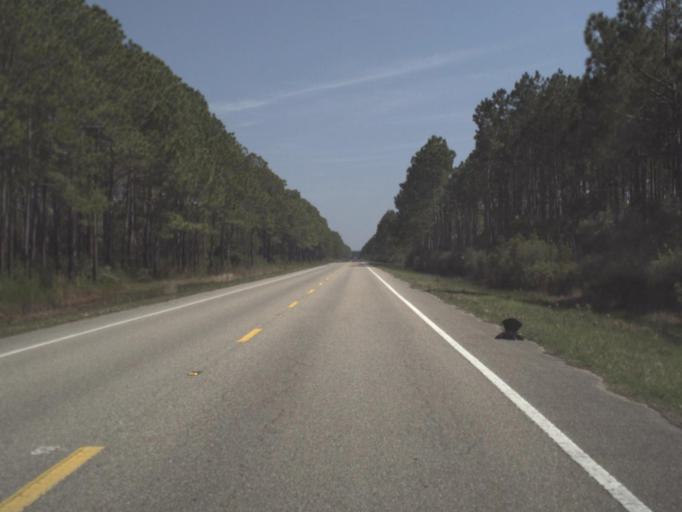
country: US
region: Florida
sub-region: Franklin County
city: Apalachicola
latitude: 29.7285
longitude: -85.1335
